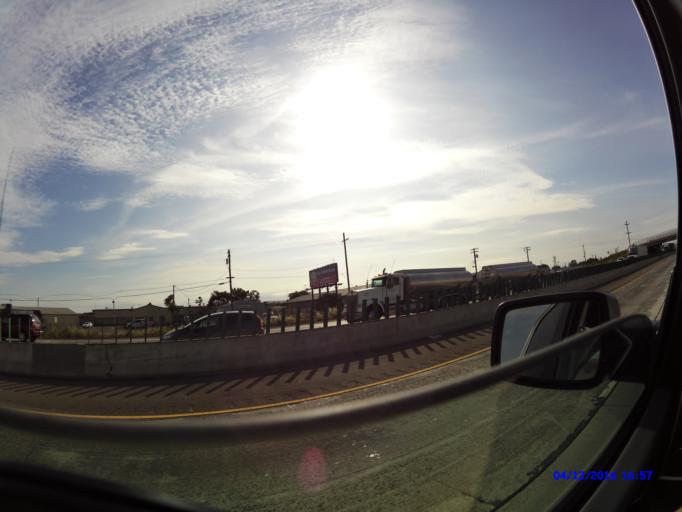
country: US
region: California
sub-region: Stanislaus County
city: Modesto
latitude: 37.6521
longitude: -121.0235
